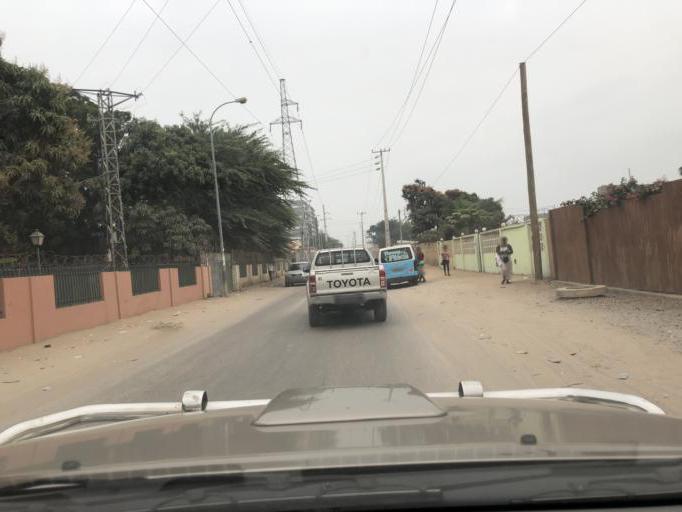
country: AO
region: Luanda
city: Luanda
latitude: -8.8863
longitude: 13.1851
